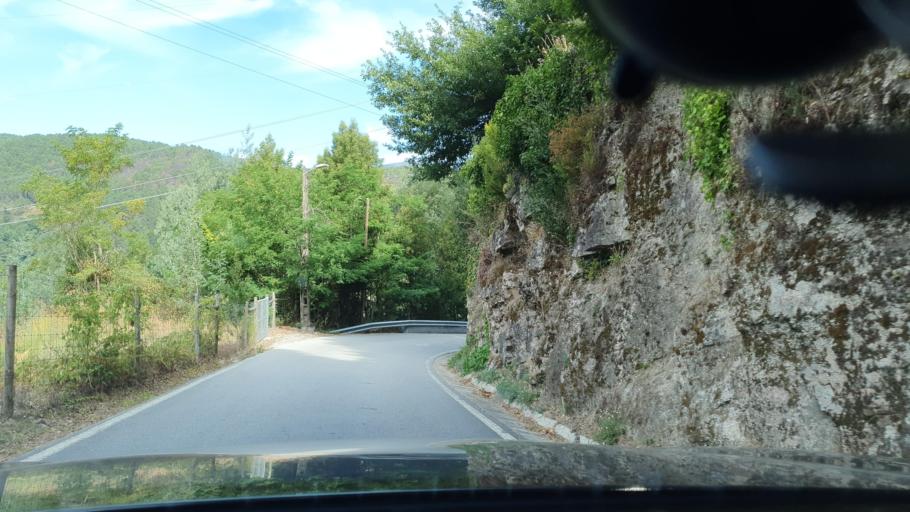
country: PT
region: Braga
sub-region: Vieira do Minho
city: Vieira do Minho
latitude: 41.6895
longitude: -8.0896
